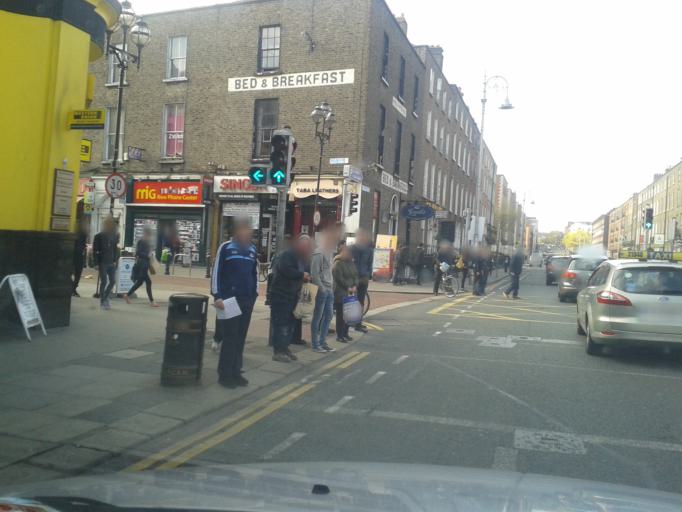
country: IE
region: Leinster
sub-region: Dublin City
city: Dublin
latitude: 53.3506
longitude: -6.2544
